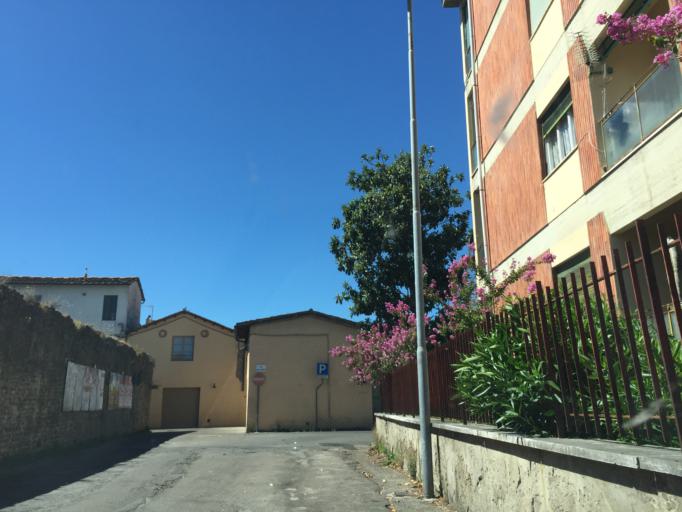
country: IT
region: Tuscany
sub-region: Provincia di Pistoia
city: Pistoia
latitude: 43.9374
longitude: 10.9208
